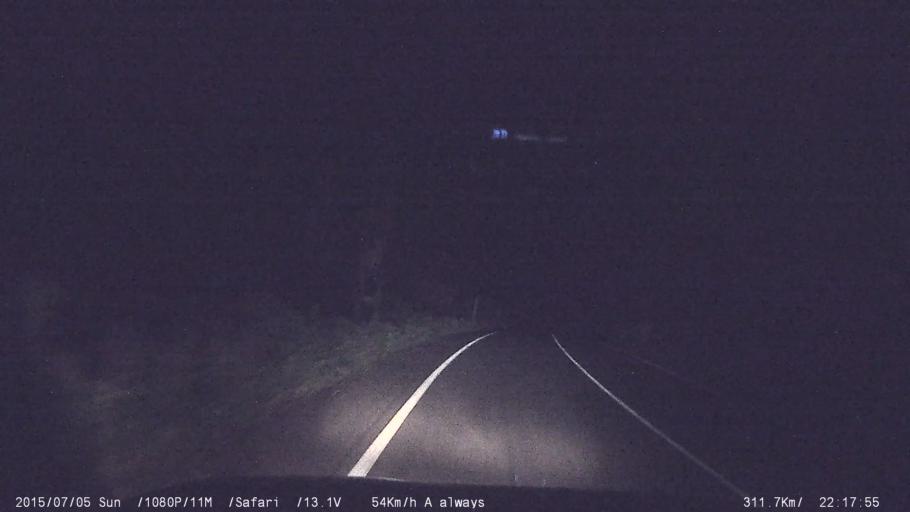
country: IN
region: Kerala
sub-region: Palakkad district
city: Palakkad
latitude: 10.8523
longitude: 76.5752
